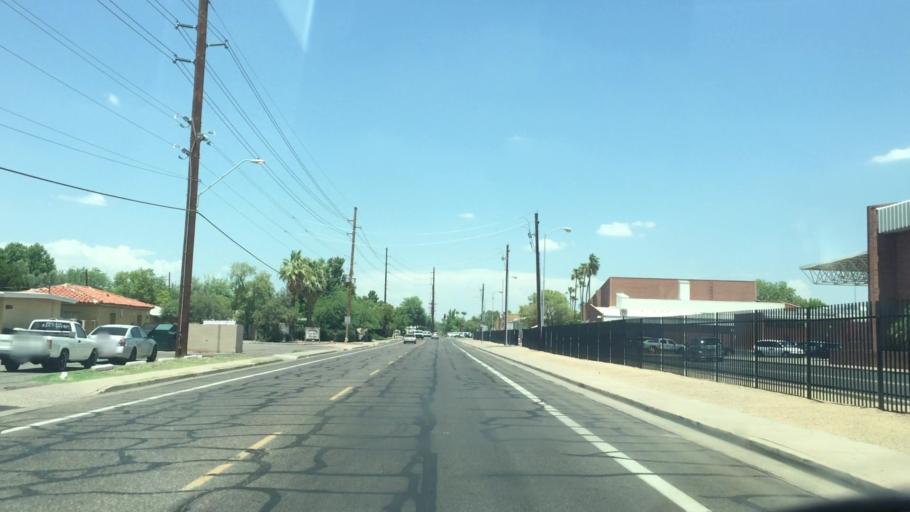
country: US
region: Arizona
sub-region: Maricopa County
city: Glendale
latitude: 33.5364
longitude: -112.1082
